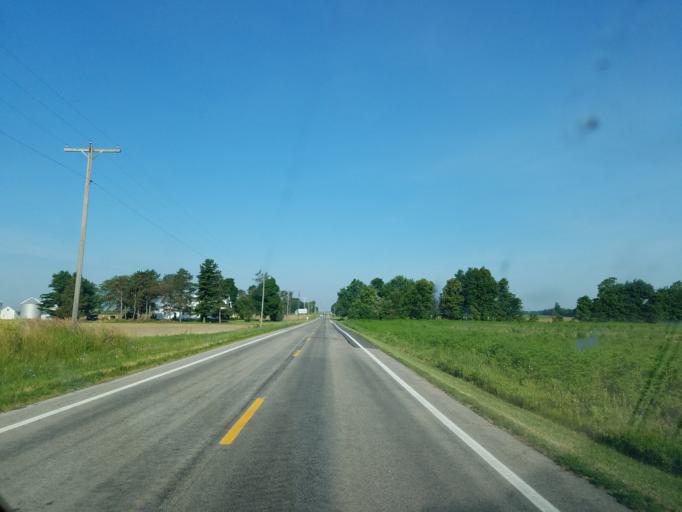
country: US
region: Ohio
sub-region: Hardin County
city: Kenton
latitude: 40.7318
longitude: -83.6365
